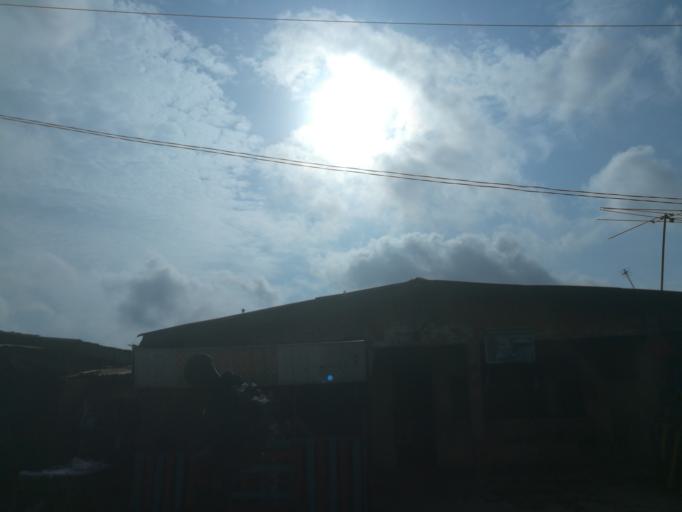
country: NG
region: Lagos
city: Agege
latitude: 6.6196
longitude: 3.3128
